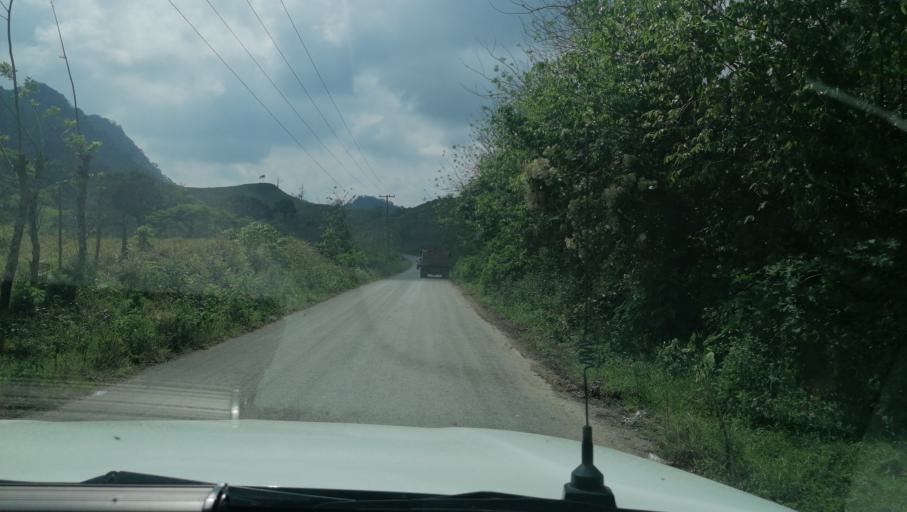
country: MX
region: Chiapas
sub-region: Francisco Leon
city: San Miguel la Sardina
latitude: 17.2520
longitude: -93.2771
